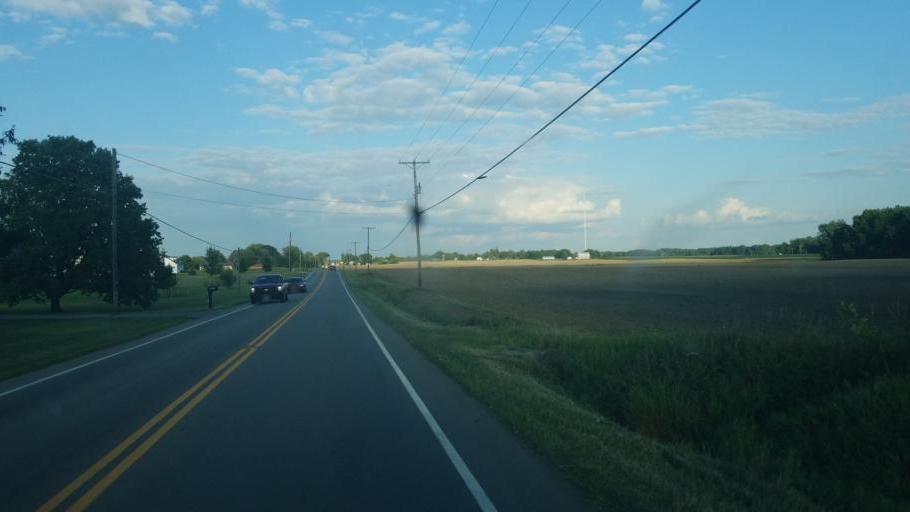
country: US
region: Ohio
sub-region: Huron County
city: Willard
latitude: 41.0527
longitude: -82.6971
